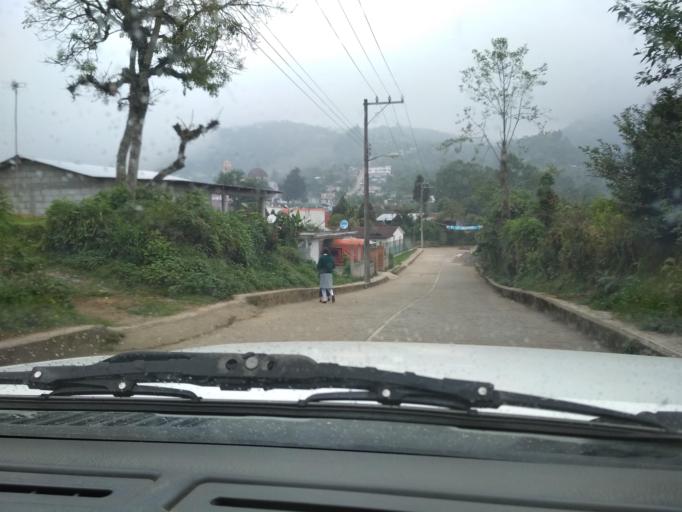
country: MX
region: Veracruz
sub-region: La Perla
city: Chilapa
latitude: 18.9882
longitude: -97.1494
